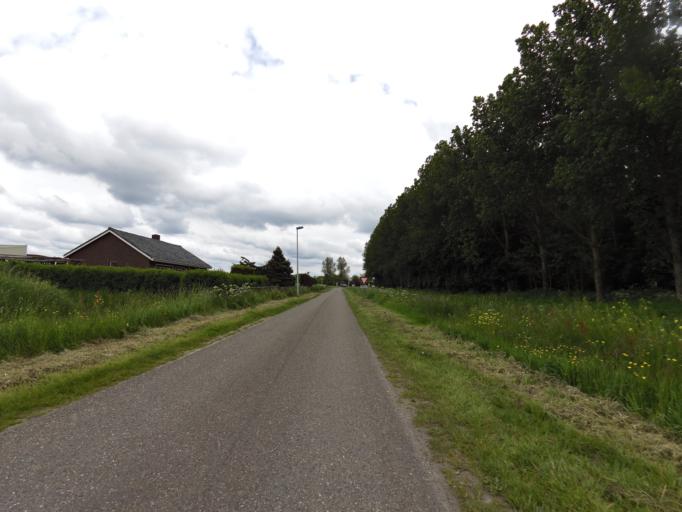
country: NL
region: South Holland
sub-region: Gemeente Brielle
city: Brielle
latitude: 51.9006
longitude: 4.1116
